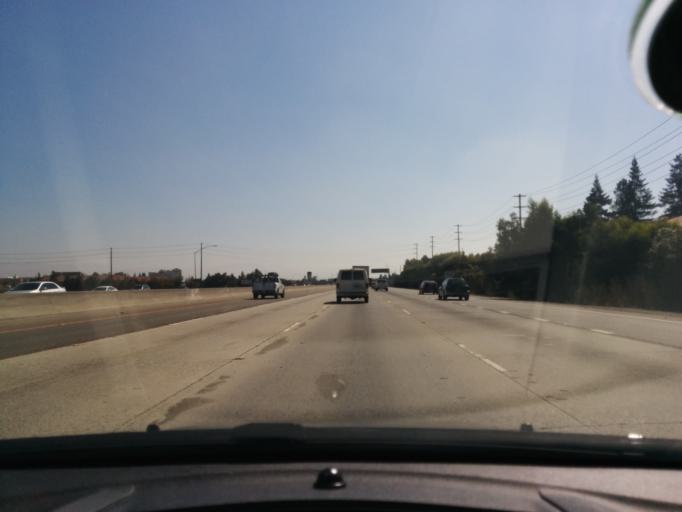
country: US
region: California
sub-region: Santa Clara County
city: Santa Clara
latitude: 37.3842
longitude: -121.9717
